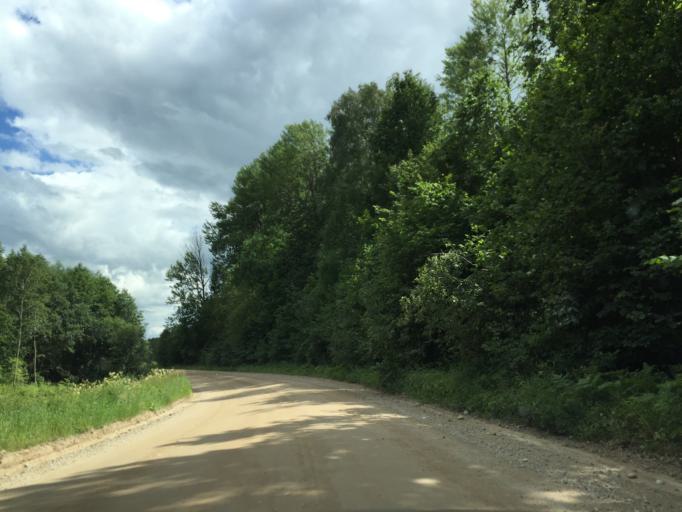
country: LV
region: Ropazu
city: Ropazi
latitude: 56.9093
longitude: 24.7662
